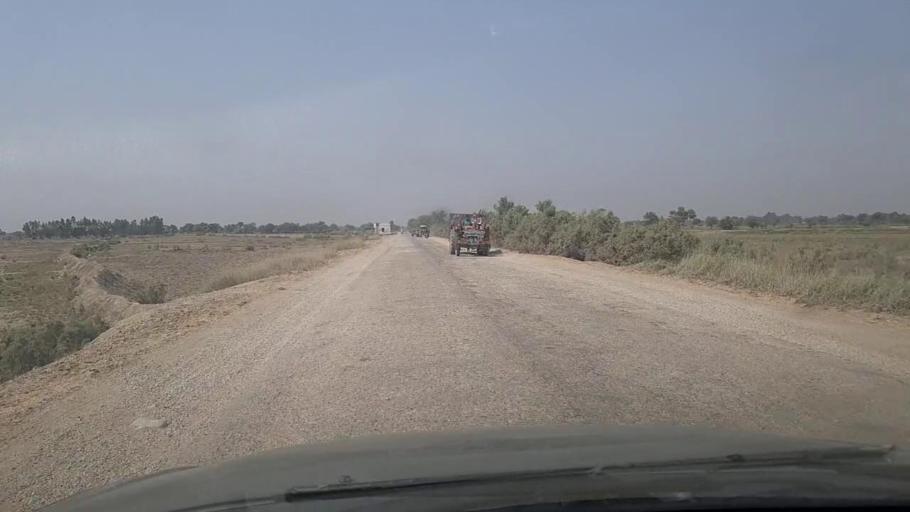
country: PK
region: Sindh
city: Khanpur
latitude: 27.9034
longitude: 69.5011
